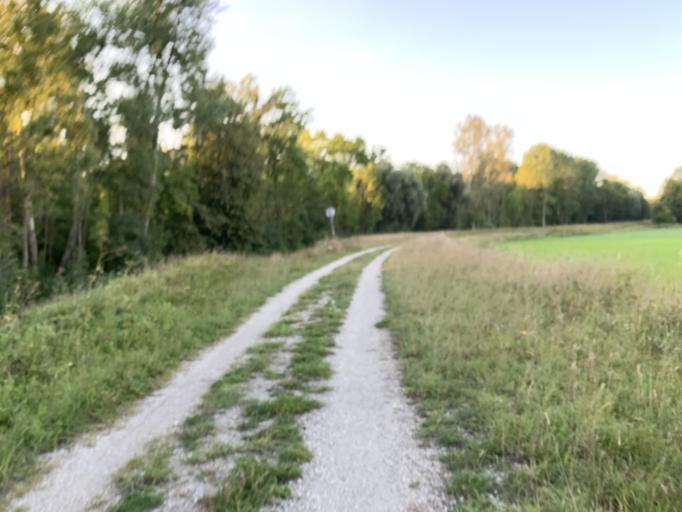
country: DE
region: Bavaria
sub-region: Upper Bavaria
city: Freising
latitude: 48.3814
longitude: 11.7441
